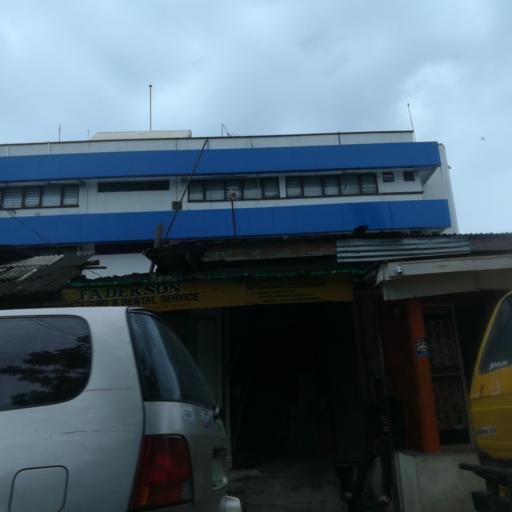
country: NG
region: Lagos
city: Ebute Metta
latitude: 6.4877
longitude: 3.3826
